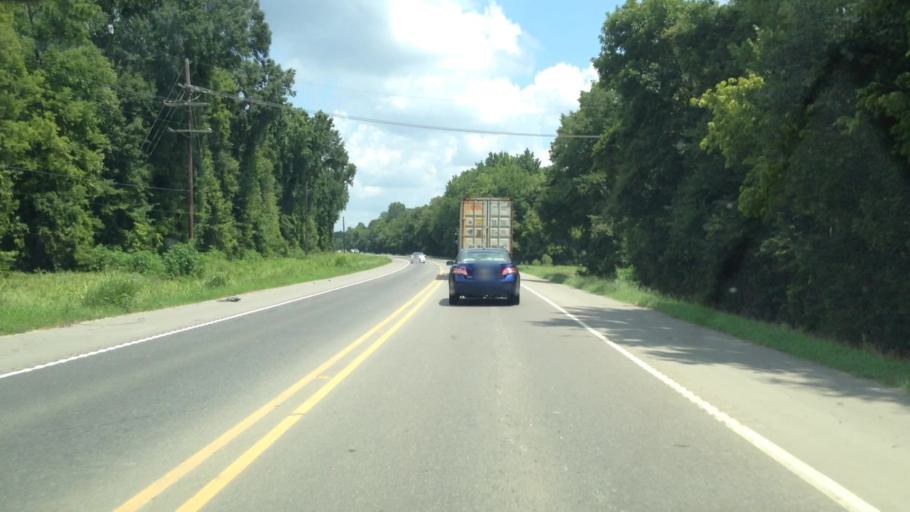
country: US
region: Louisiana
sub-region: Ascension Parish
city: Sorrento
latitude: 30.1519
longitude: -90.8748
